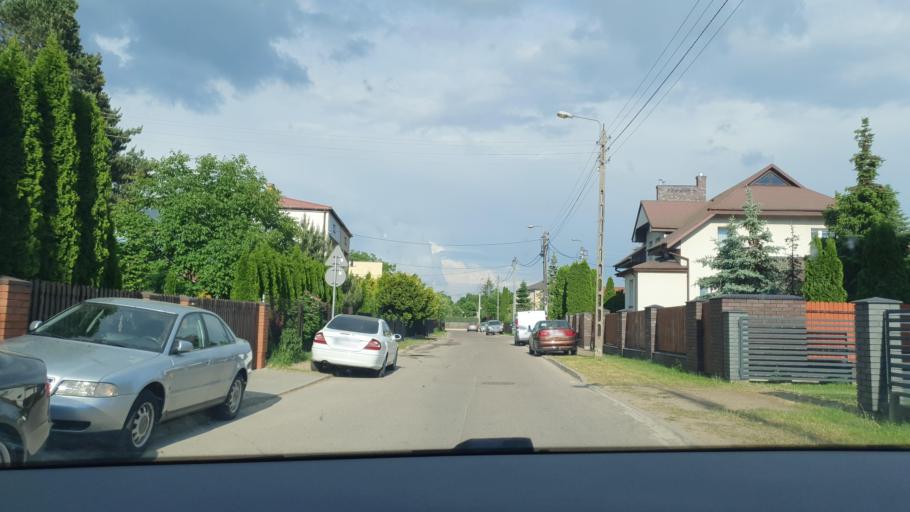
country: PL
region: Podlasie
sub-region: Powiat bialostocki
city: Wasilkow
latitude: 53.1274
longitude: 23.2559
